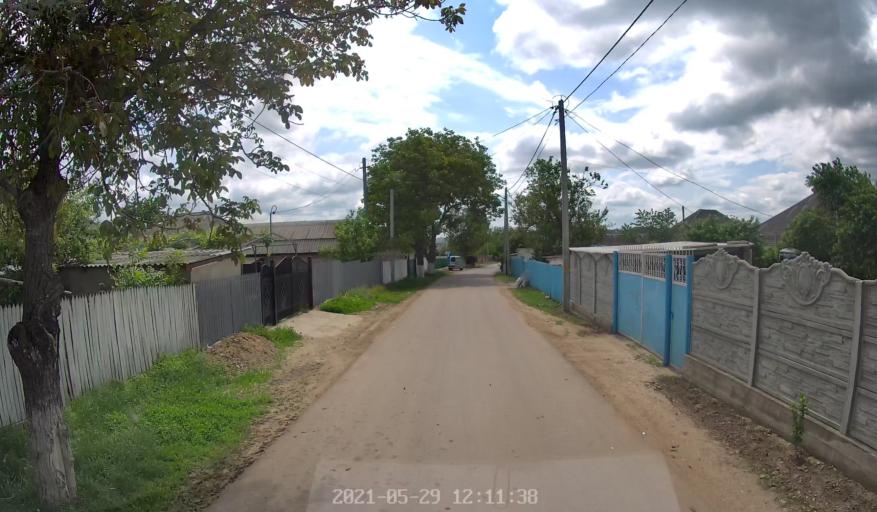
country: MD
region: Hincesti
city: Hincesti
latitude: 46.8823
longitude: 28.6302
